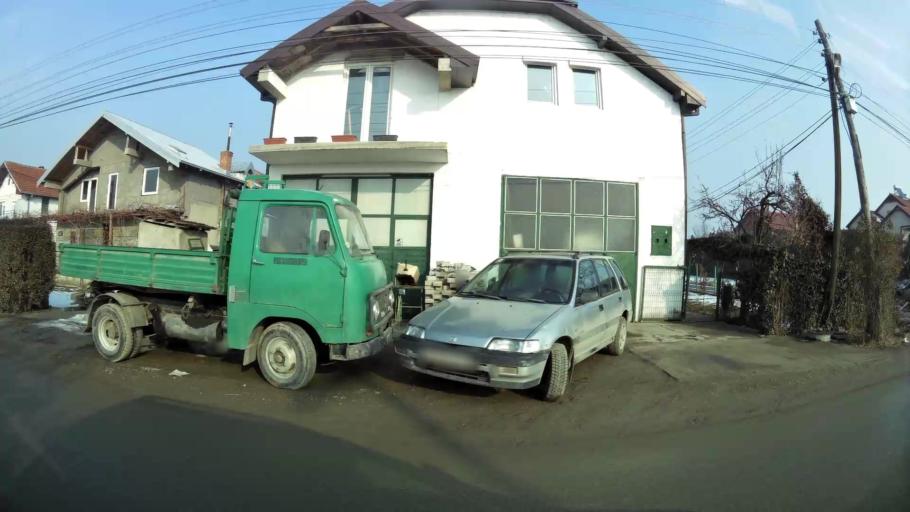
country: MK
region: Ilinden
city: Marino
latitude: 41.9825
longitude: 21.5916
